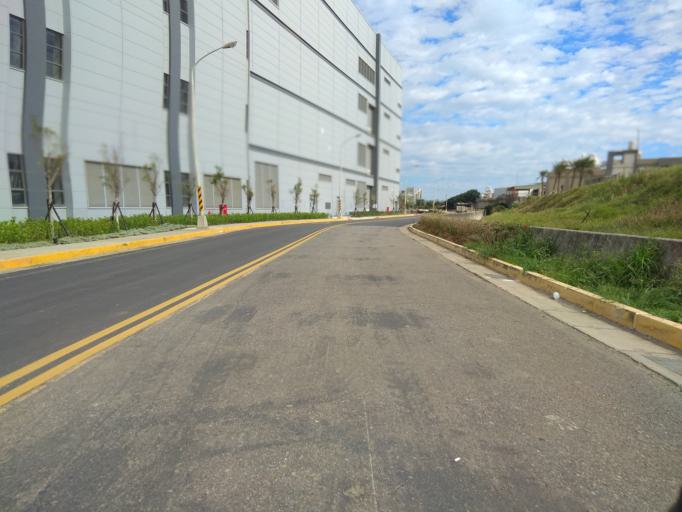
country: TW
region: Taiwan
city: Taoyuan City
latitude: 25.0503
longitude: 121.0926
